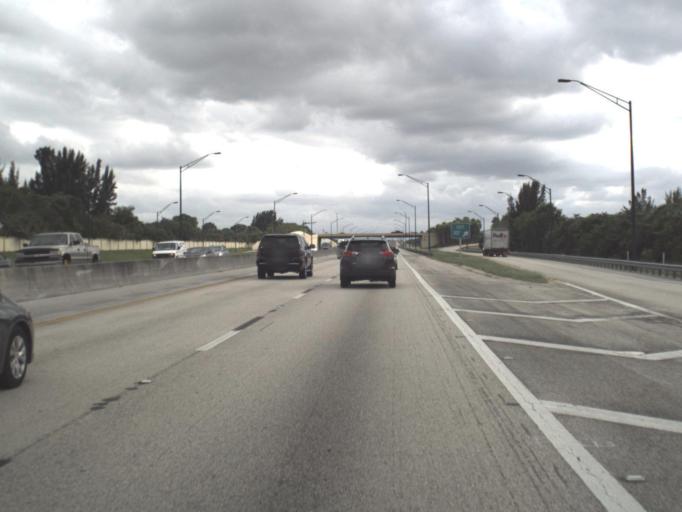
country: US
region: Florida
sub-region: Palm Beach County
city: Palm Beach Gardens
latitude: 26.8078
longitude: -80.1313
